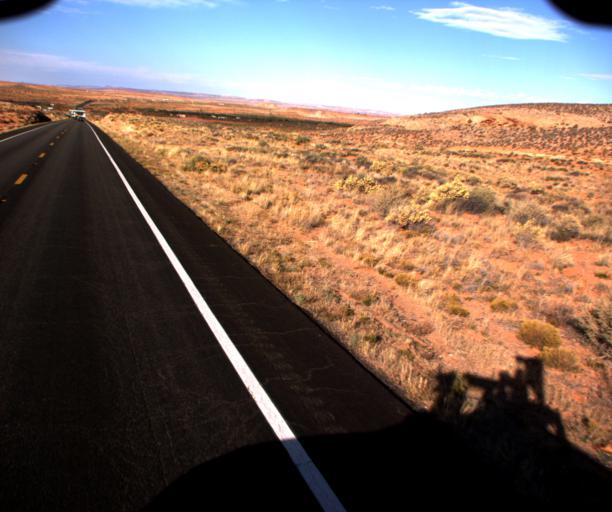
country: US
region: Arizona
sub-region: Apache County
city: Many Farms
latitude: 36.9251
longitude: -109.5942
